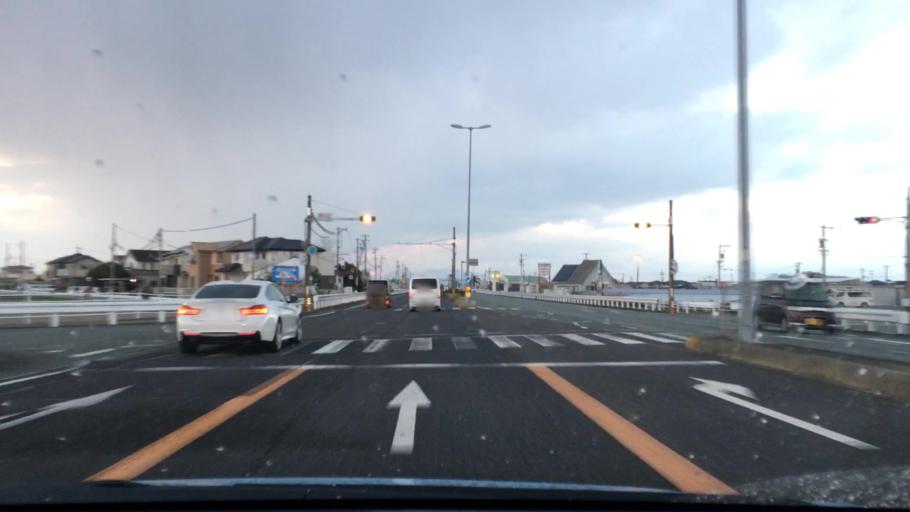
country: JP
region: Mie
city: Ise
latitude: 34.5654
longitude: 136.6380
